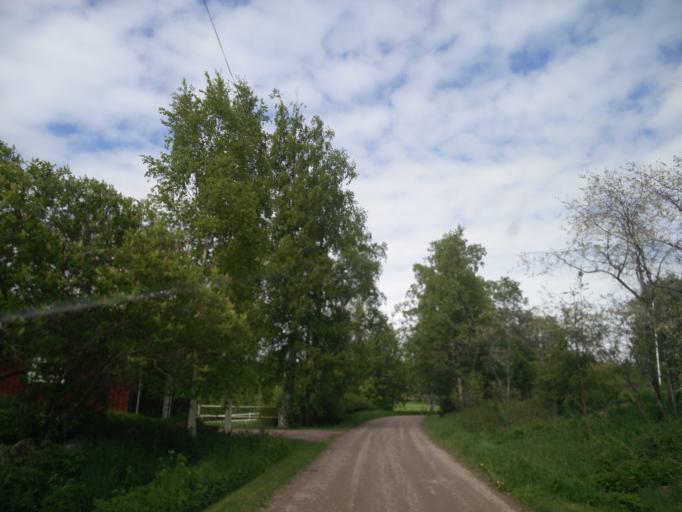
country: SE
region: Vaesternorrland
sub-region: Sundsvalls Kommun
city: Njurundabommen
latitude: 62.2252
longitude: 17.3573
